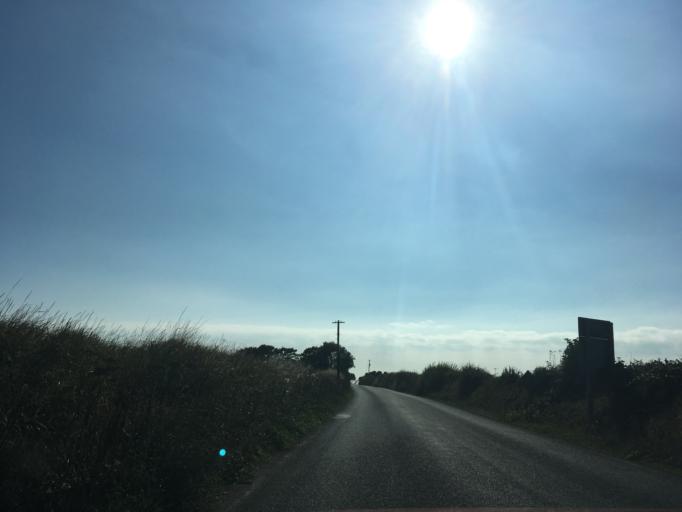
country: IE
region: Leinster
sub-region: Loch Garman
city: Rosslare
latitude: 52.2269
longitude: -6.4421
